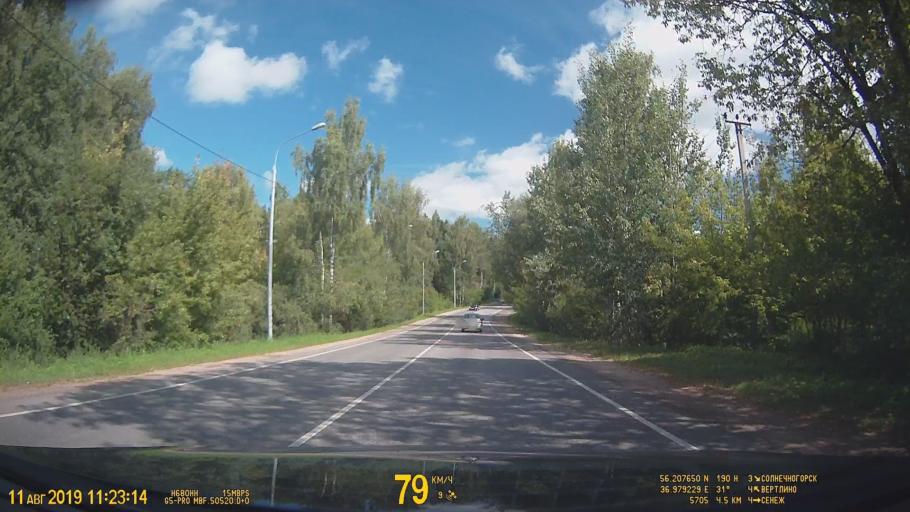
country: RU
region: Moskovskaya
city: Solnechnogorsk
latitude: 56.2079
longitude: 36.9795
